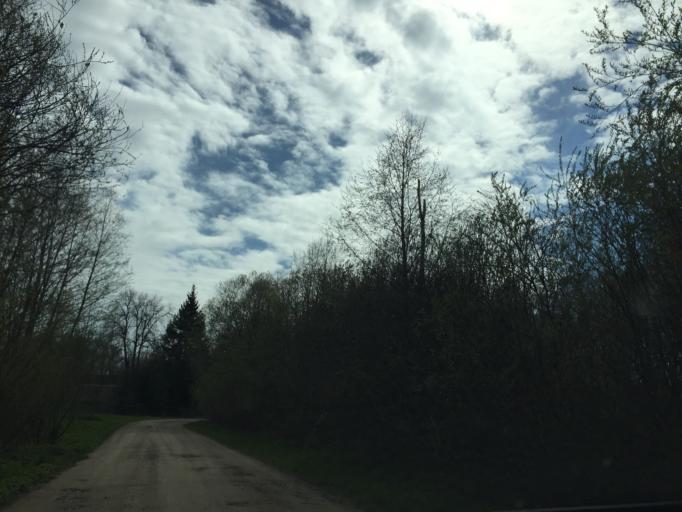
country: LV
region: Ozolnieku
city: Ozolnieki
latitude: 56.5821
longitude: 23.7941
